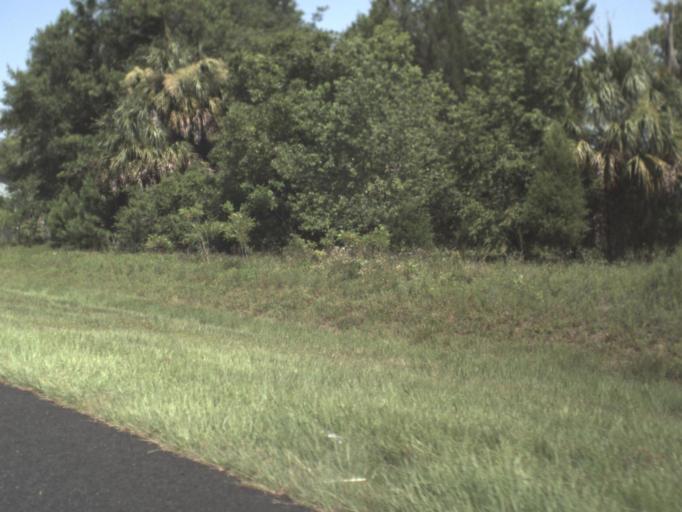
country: US
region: Florida
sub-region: Levy County
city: Manatee Road
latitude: 29.5837
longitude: -82.9517
